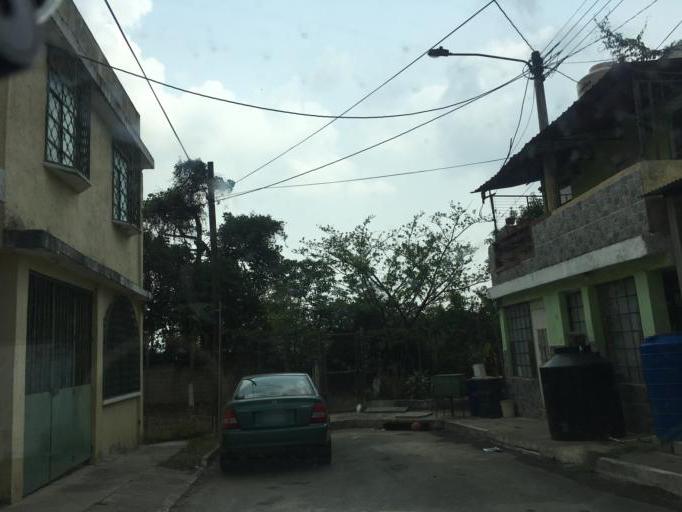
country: GT
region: Guatemala
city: Petapa
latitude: 14.5069
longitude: -90.5530
